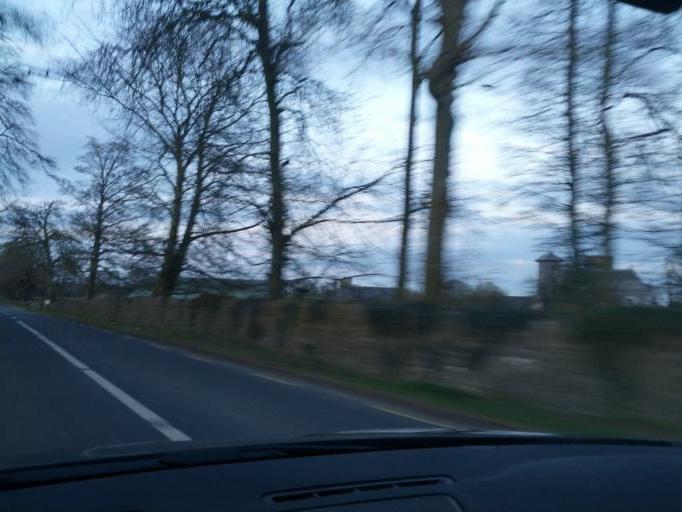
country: IE
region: Connaught
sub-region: County Galway
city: Portumna
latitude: 53.0284
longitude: -8.1214
